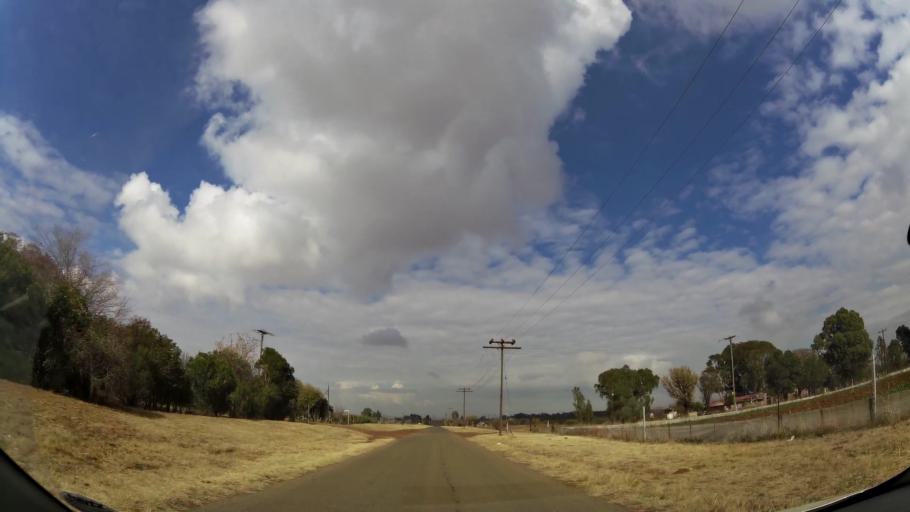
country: ZA
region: Gauteng
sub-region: Sedibeng District Municipality
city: Meyerton
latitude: -26.6199
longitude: 28.0757
